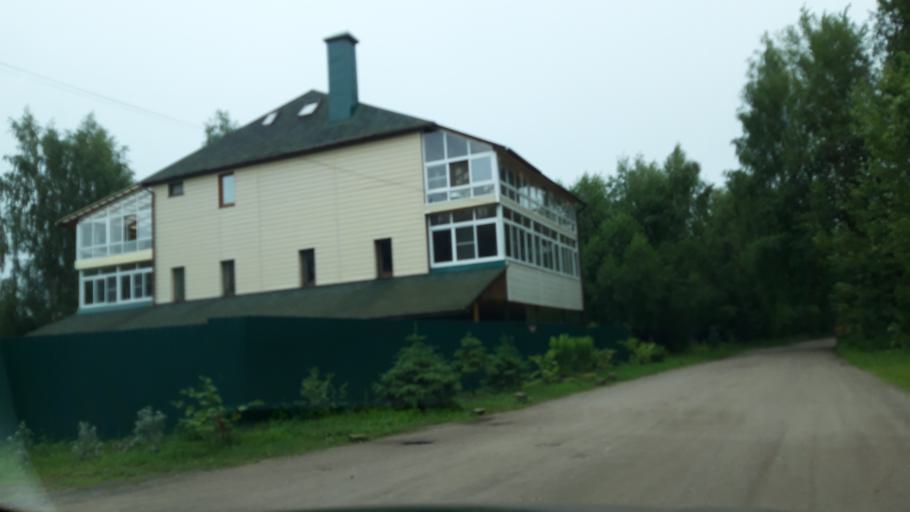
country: RU
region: Tverskaya
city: Konakovo
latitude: 56.6563
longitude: 36.6553
